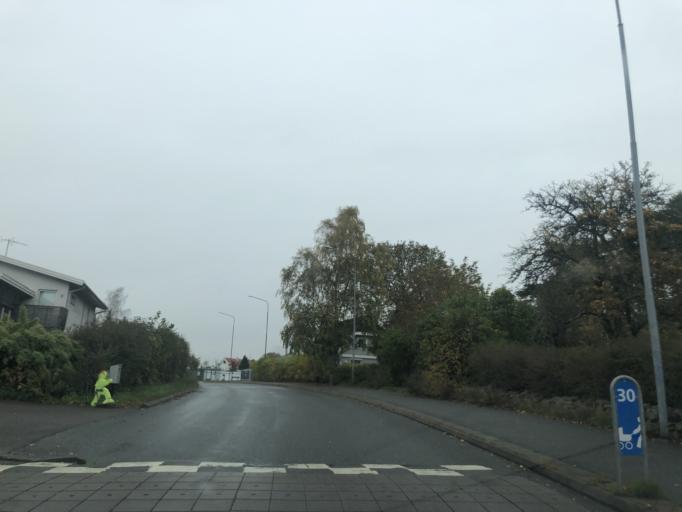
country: SE
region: Vaestra Goetaland
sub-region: Goteborg
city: Majorna
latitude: 57.6308
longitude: 11.9234
